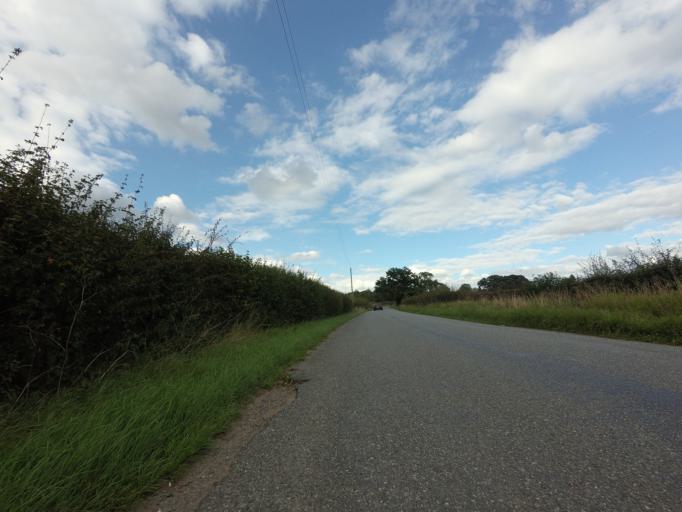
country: GB
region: England
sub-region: Kent
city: Marden
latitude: 51.2118
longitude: 0.5083
